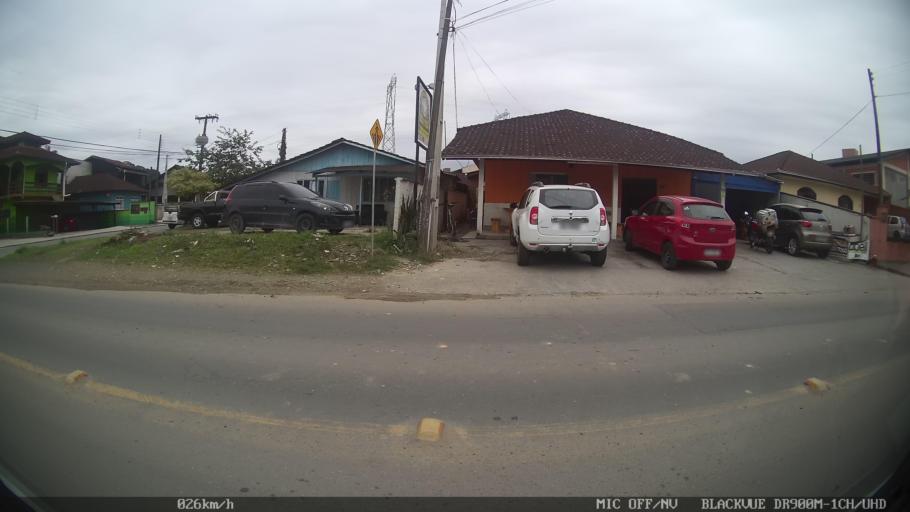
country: BR
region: Santa Catarina
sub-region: Joinville
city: Joinville
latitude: -26.2678
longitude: -48.8909
